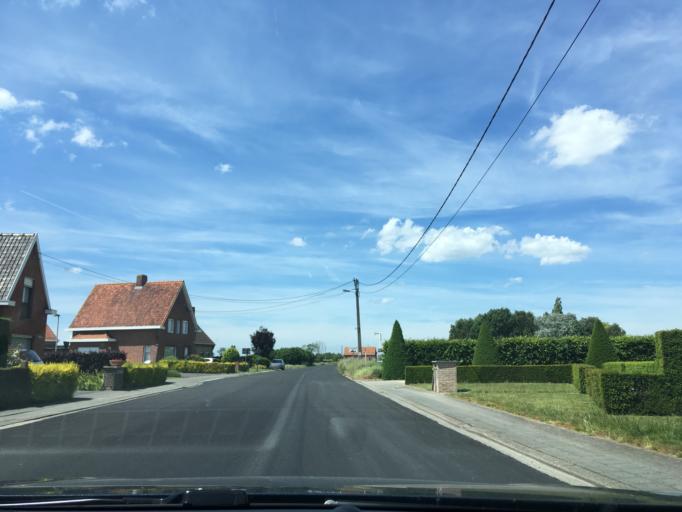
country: BE
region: Flanders
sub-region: Provincie West-Vlaanderen
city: Ardooie
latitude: 51.0039
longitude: 3.2035
